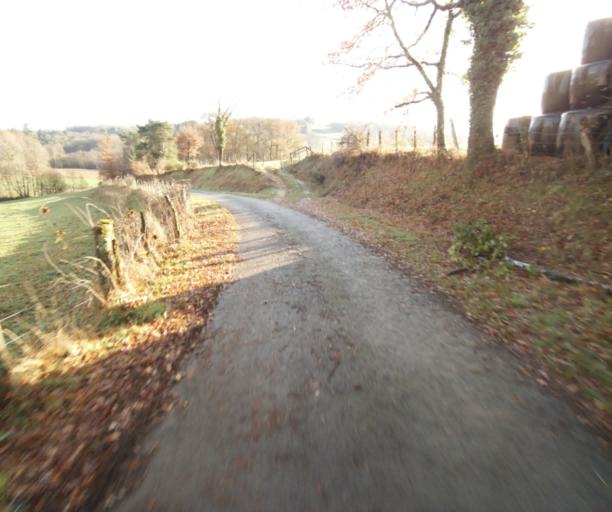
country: FR
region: Limousin
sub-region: Departement de la Correze
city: Saint-Mexant
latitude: 45.2406
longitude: 1.6409
